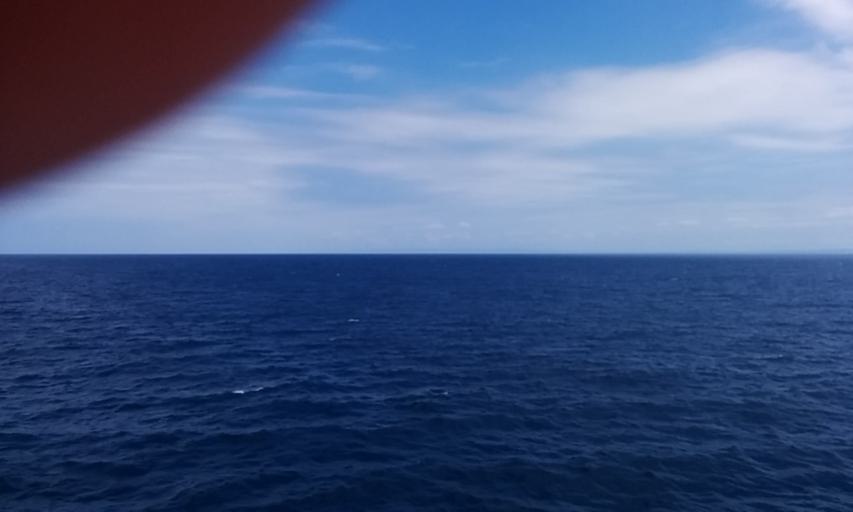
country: JP
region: Kagoshima
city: Nishinoomote
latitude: 30.5144
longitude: 130.6116
